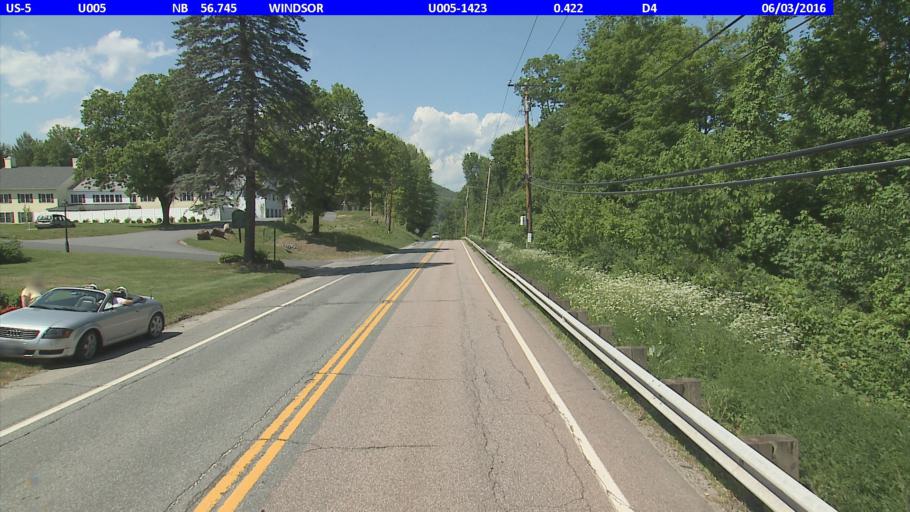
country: US
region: Vermont
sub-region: Windsor County
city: Windsor
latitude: 43.4348
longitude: -72.3965
